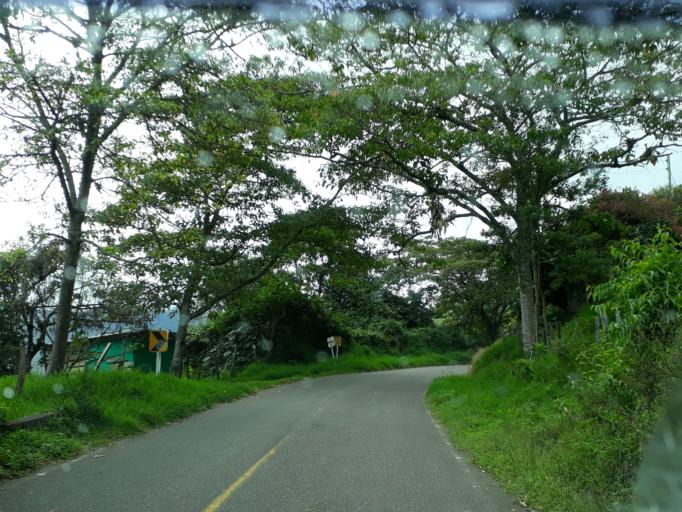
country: CO
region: Cundinamarca
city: Cabrera
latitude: 4.0225
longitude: -74.5118
